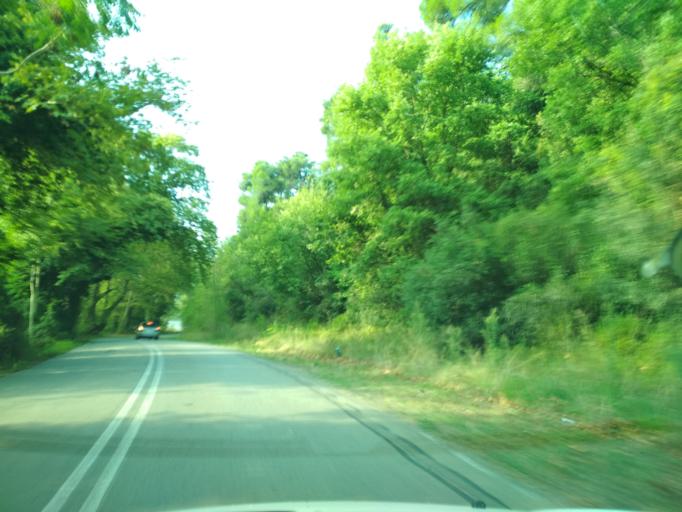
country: GR
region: Central Greece
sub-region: Nomos Evvoias
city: Mantoudi
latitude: 38.7846
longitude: 23.4706
